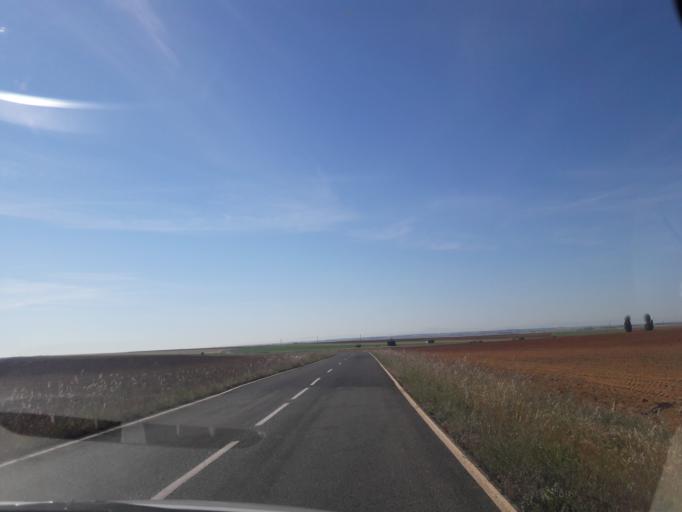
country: ES
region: Castille and Leon
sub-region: Provincia de Salamanca
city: Aldeanueva de Figueroa
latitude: 41.1431
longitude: -5.5119
